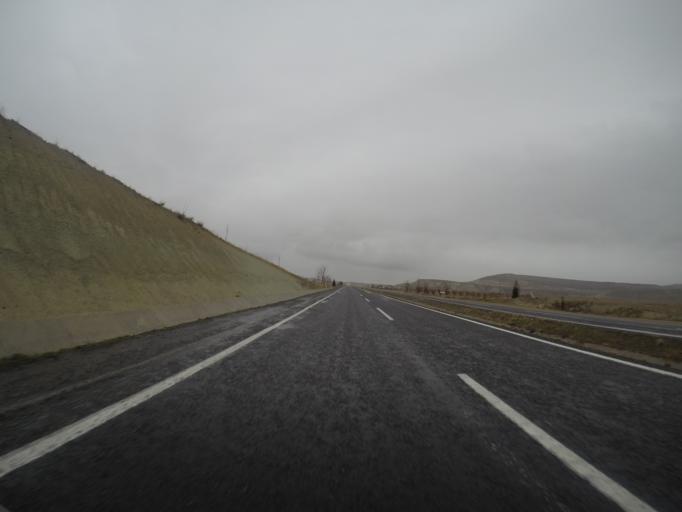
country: TR
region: Nevsehir
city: Urgub
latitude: 38.7298
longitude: 34.9650
